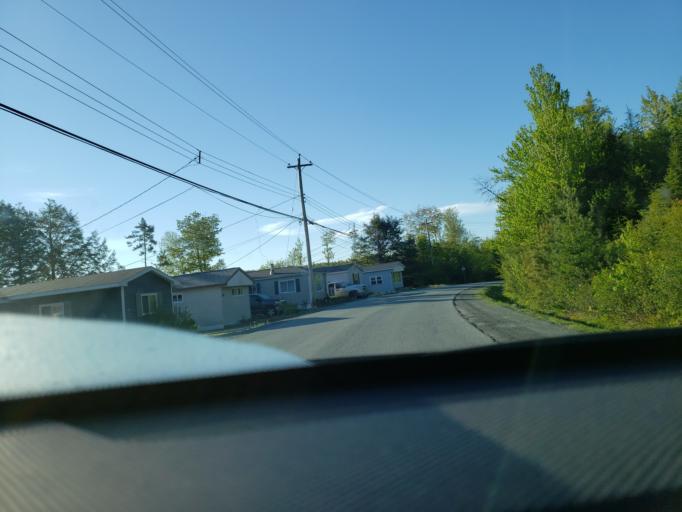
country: CA
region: Nova Scotia
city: Cole Harbour
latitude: 44.7448
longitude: -63.3808
